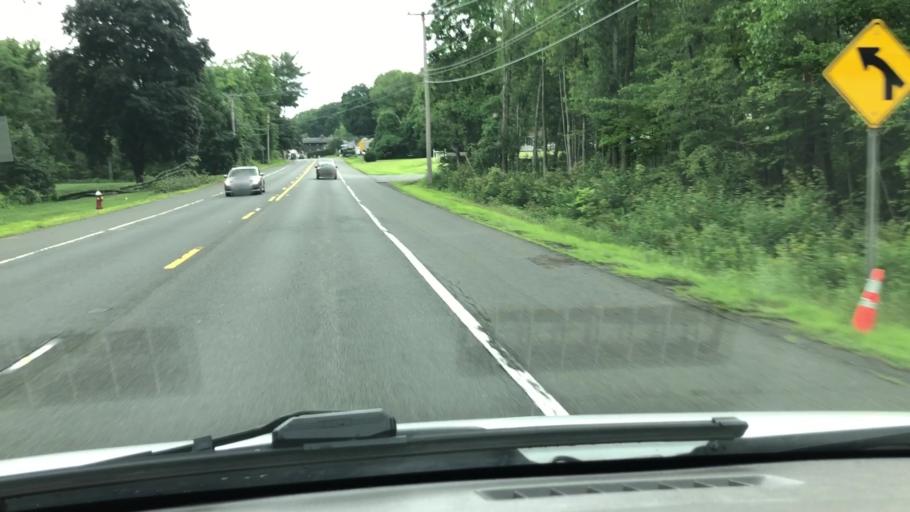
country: US
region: Massachusetts
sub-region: Hampshire County
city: Hatfield
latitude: 42.3954
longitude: -72.6313
